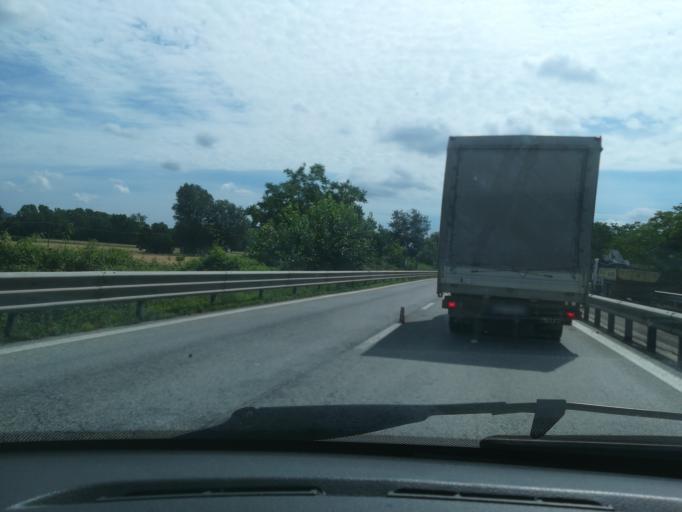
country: IT
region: The Marches
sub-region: Provincia di Macerata
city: Corridonia
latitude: 43.2687
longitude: 13.5142
